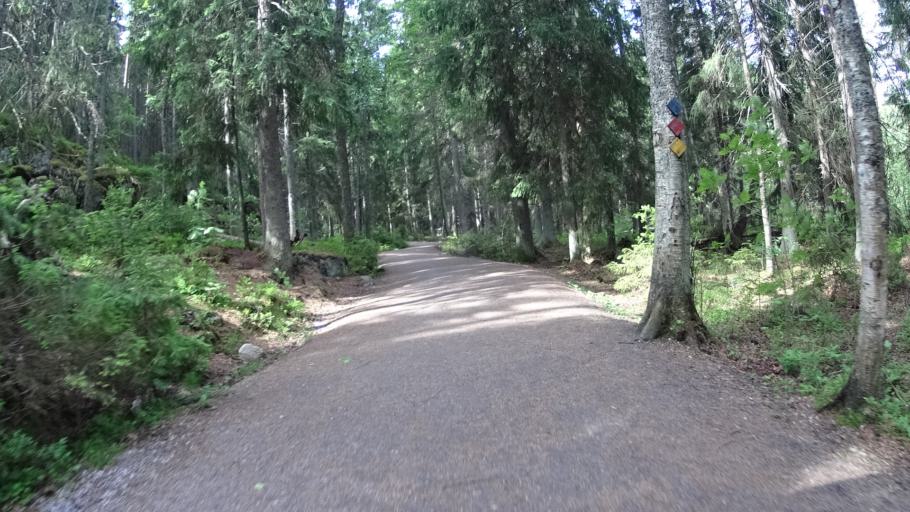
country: FI
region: Uusimaa
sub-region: Helsinki
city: Espoo
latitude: 60.3088
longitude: 24.5133
